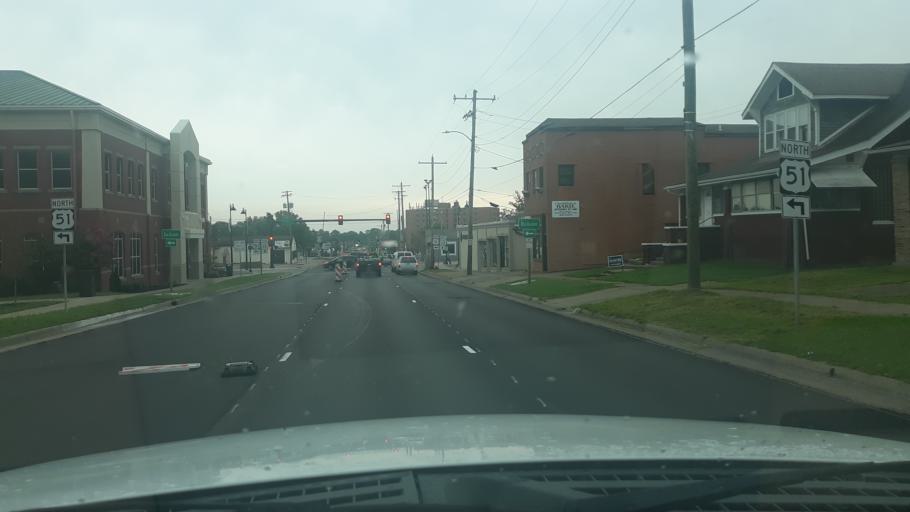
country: US
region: Illinois
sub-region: Jackson County
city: Carbondale
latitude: 37.7255
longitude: -89.2182
